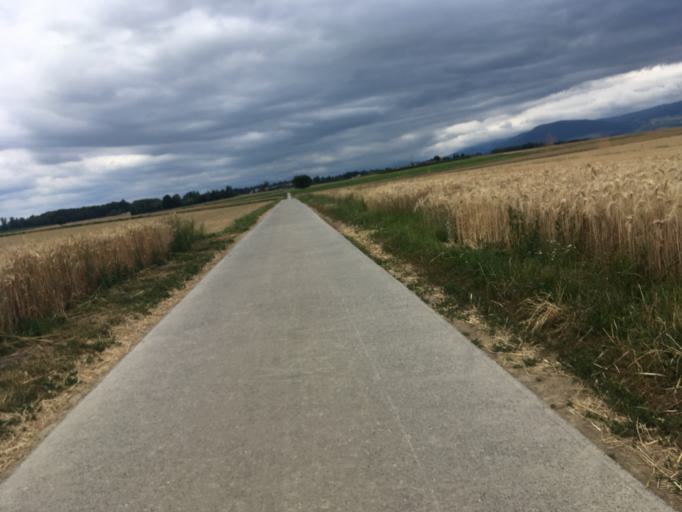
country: CH
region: Vaud
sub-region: Broye-Vully District
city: Payerne
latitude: 46.8750
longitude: 6.9196
